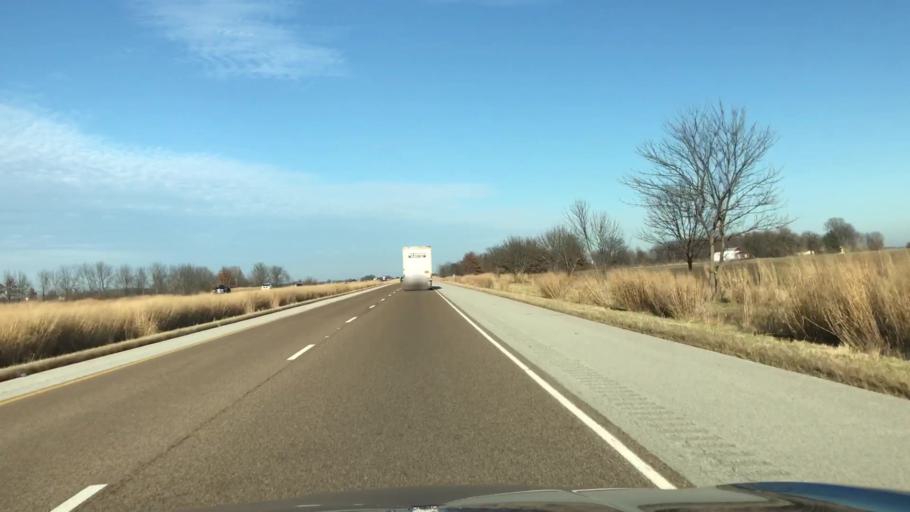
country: US
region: Illinois
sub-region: Macoupin County
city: Mount Olive
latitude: 39.1294
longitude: -89.7112
